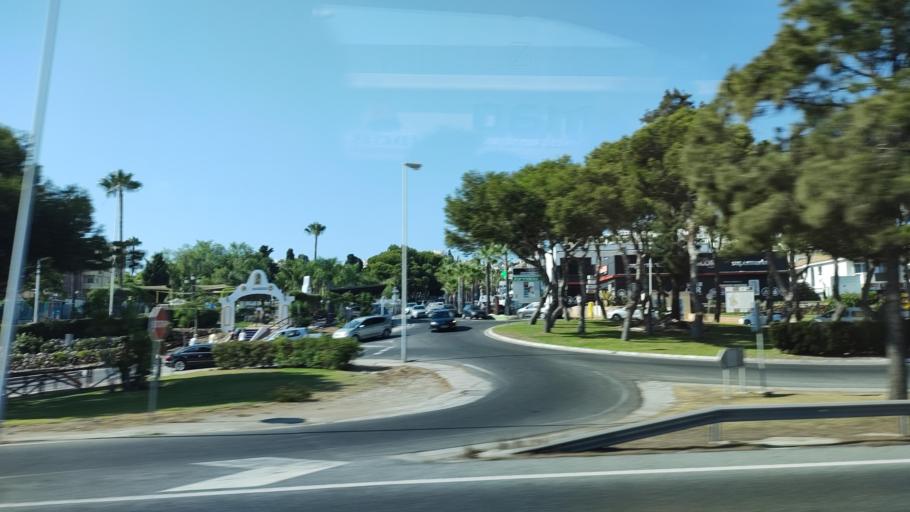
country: ES
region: Andalusia
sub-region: Provincia de Malaga
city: Fuengirola
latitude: 36.4910
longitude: -4.7058
